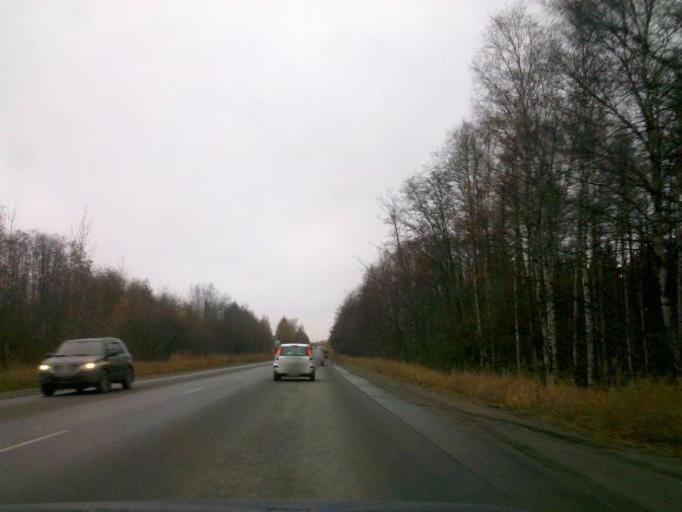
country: RU
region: Republic of Karelia
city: Petrozavodsk
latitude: 61.8215
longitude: 34.2389
